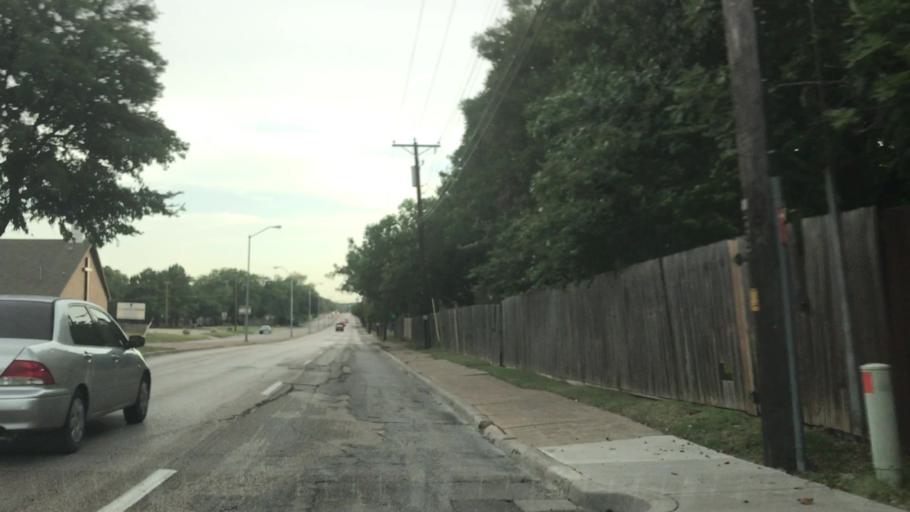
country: US
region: Texas
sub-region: Dallas County
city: Mesquite
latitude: 32.8311
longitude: -96.6374
